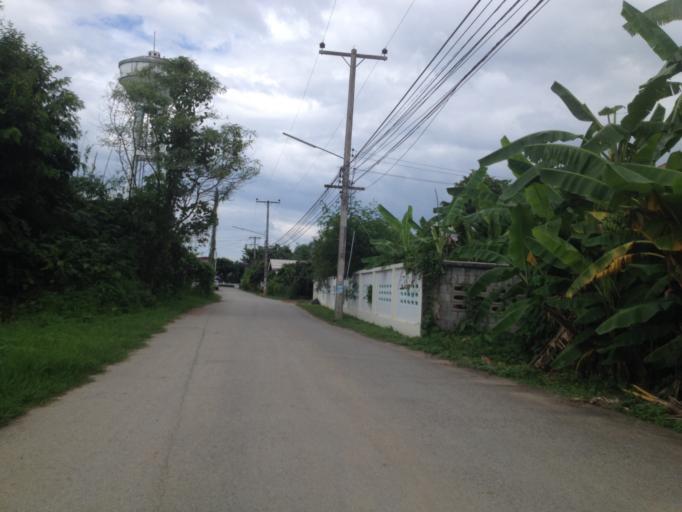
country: TH
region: Chiang Mai
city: Hang Dong
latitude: 18.6979
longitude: 98.9123
